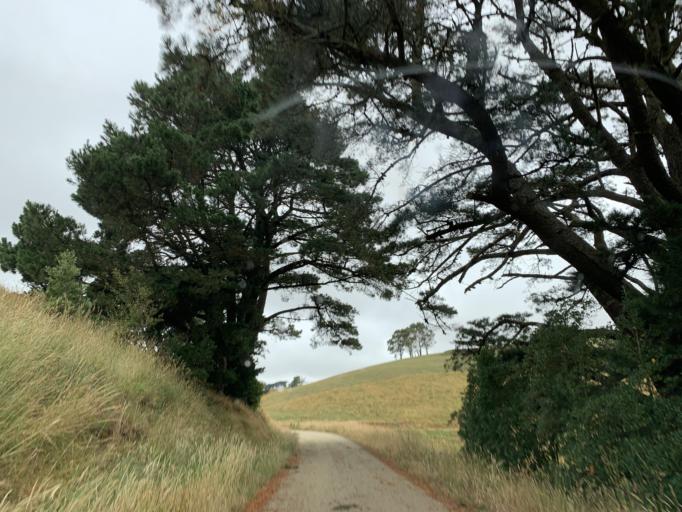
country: AU
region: Victoria
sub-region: Baw Baw
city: Warragul
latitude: -38.3003
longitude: 145.8875
